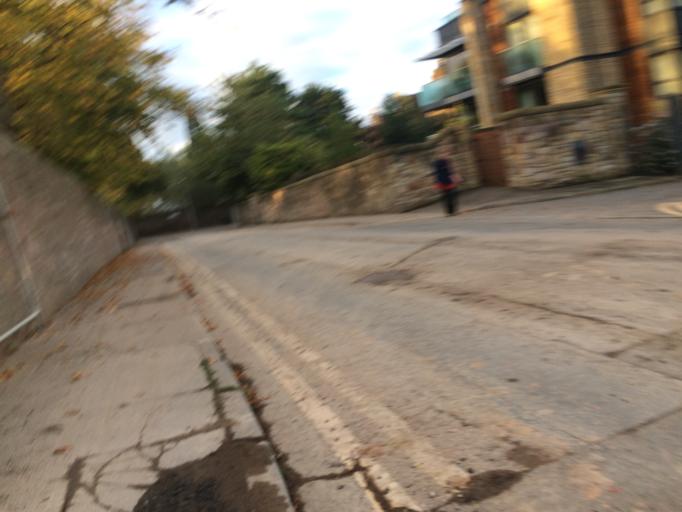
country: GB
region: Scotland
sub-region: Edinburgh
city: Edinburgh
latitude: 55.9315
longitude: -3.2046
